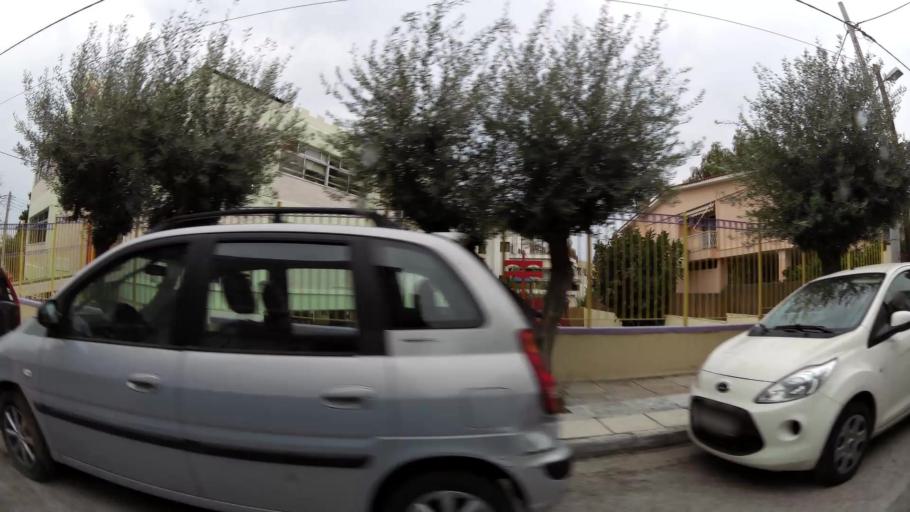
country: GR
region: Attica
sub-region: Nomarchia Athinas
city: Alimos
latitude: 37.9090
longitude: 23.7248
